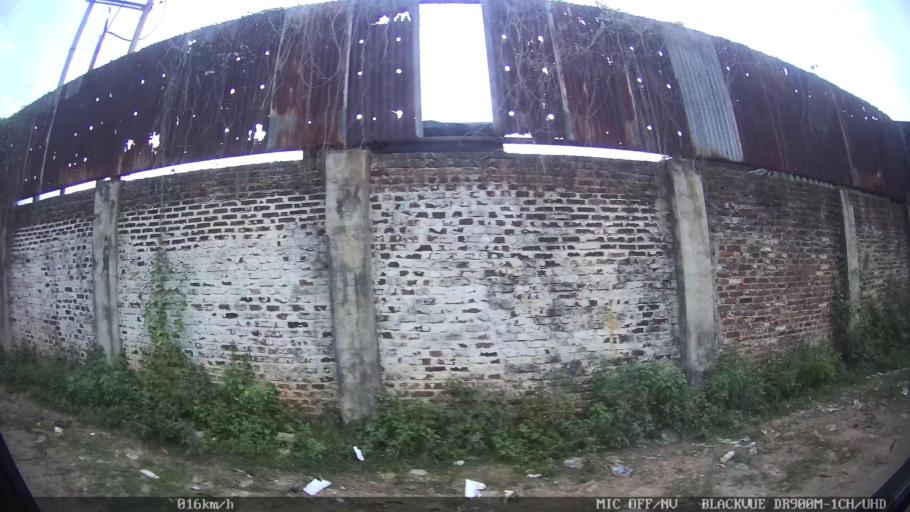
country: ID
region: Lampung
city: Bandarlampung
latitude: -5.4366
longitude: 105.2917
